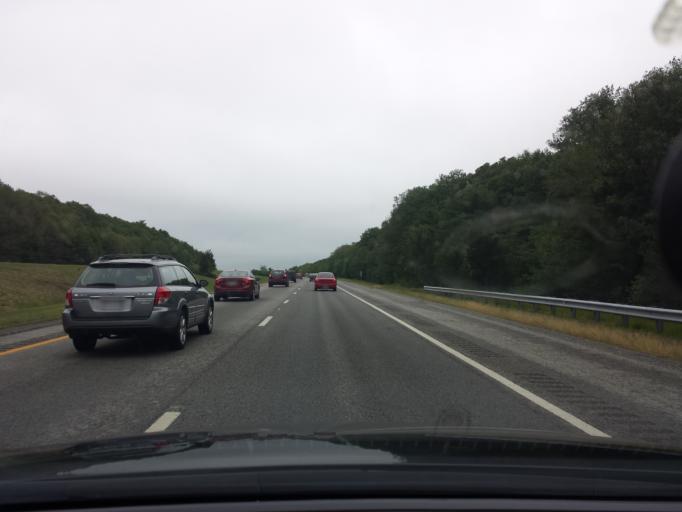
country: US
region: Rhode Island
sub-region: Kent County
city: West Greenwich
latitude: 41.6324
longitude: -71.6323
